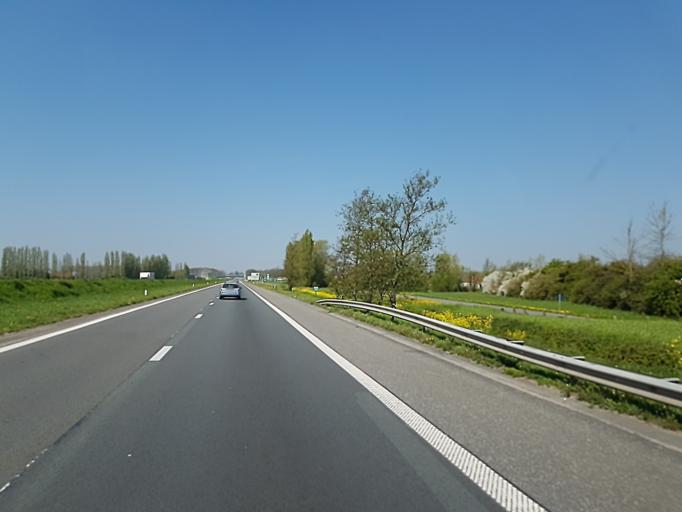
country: BE
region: Flanders
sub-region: Provincie West-Vlaanderen
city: Wervik
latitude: 50.8323
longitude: 3.0284
